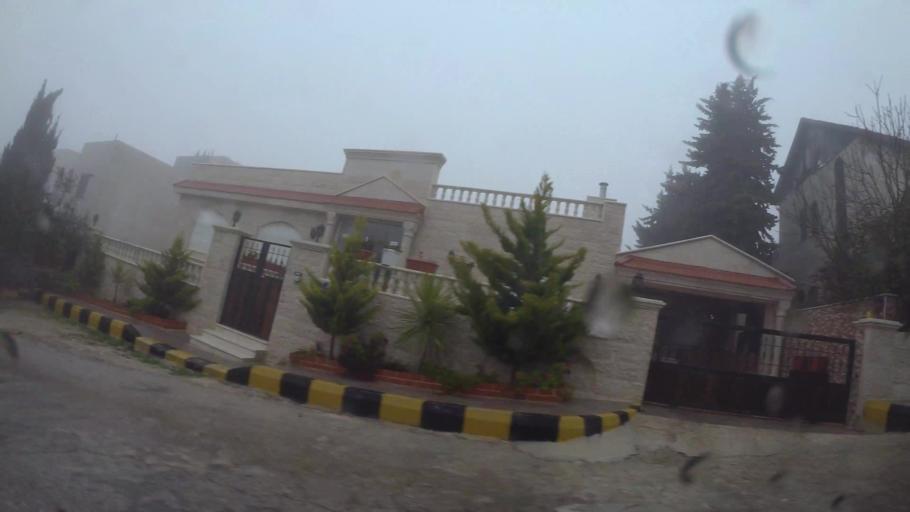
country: JO
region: Amman
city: Al Jubayhah
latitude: 32.0139
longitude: 35.8817
